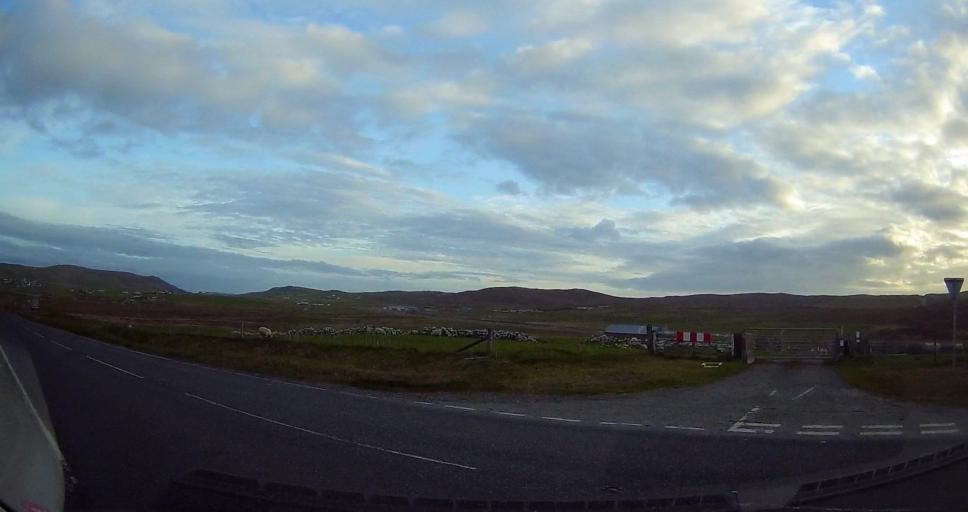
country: GB
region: Scotland
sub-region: Shetland Islands
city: Lerwick
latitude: 60.1992
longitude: -1.2325
